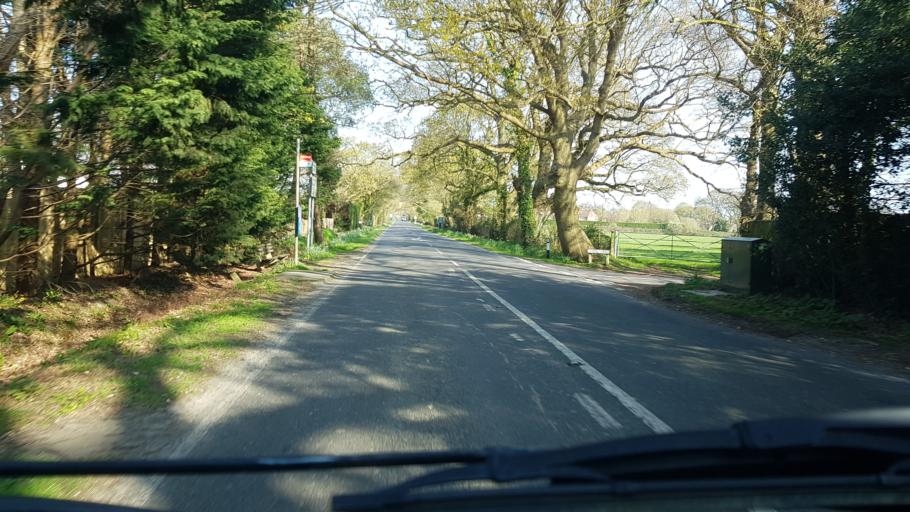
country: GB
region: England
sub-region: West Sussex
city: East Wittering
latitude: 50.7875
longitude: -0.8717
